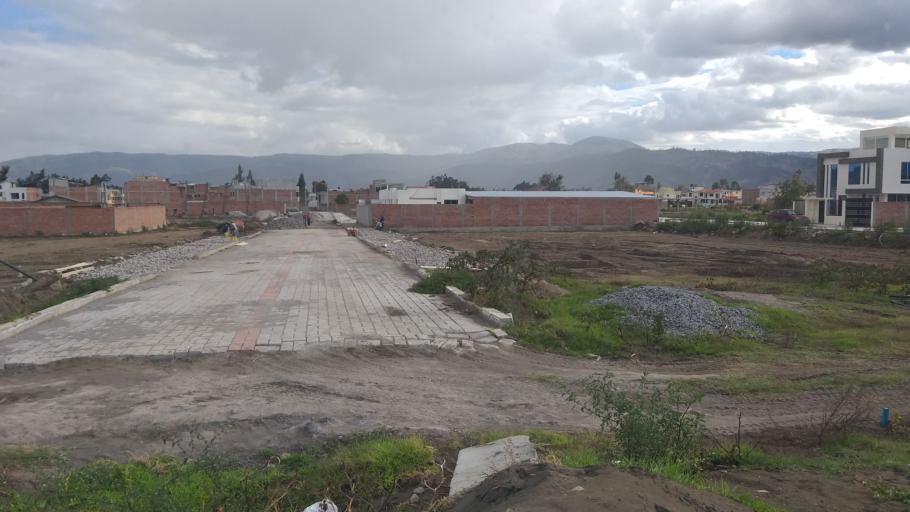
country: EC
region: Chimborazo
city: Riobamba
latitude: -1.6864
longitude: -78.6234
